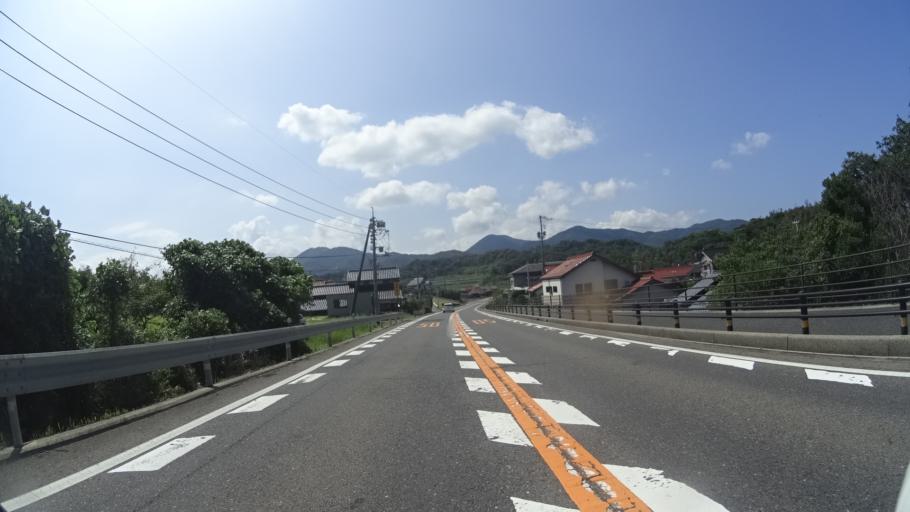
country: JP
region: Shimane
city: Masuda
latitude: 34.6736
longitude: 131.7528
